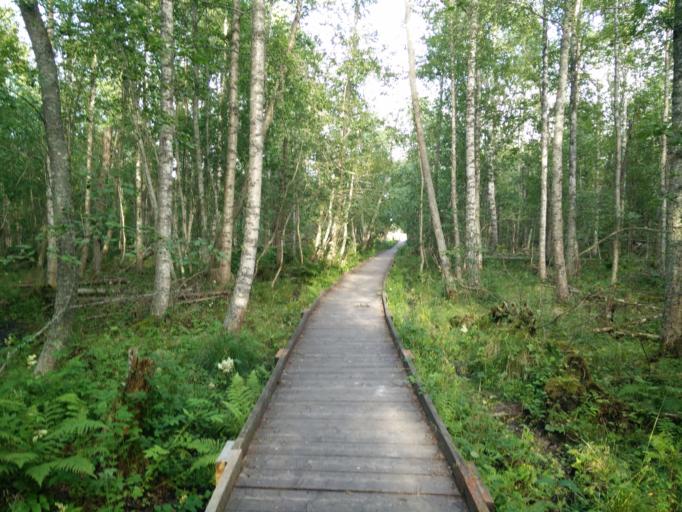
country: SE
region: Vaesternorrland
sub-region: Timra Kommun
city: Soraker
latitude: 62.4506
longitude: 17.4871
